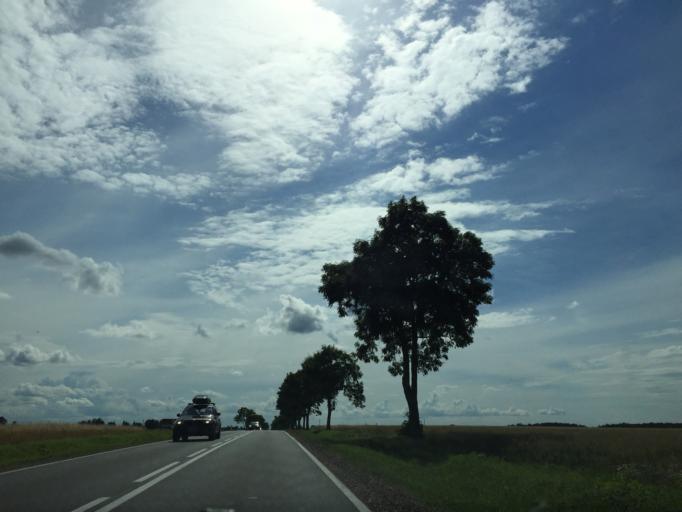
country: PL
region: Masovian Voivodeship
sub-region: Powiat losicki
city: Losice
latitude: 52.2290
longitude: 22.7536
